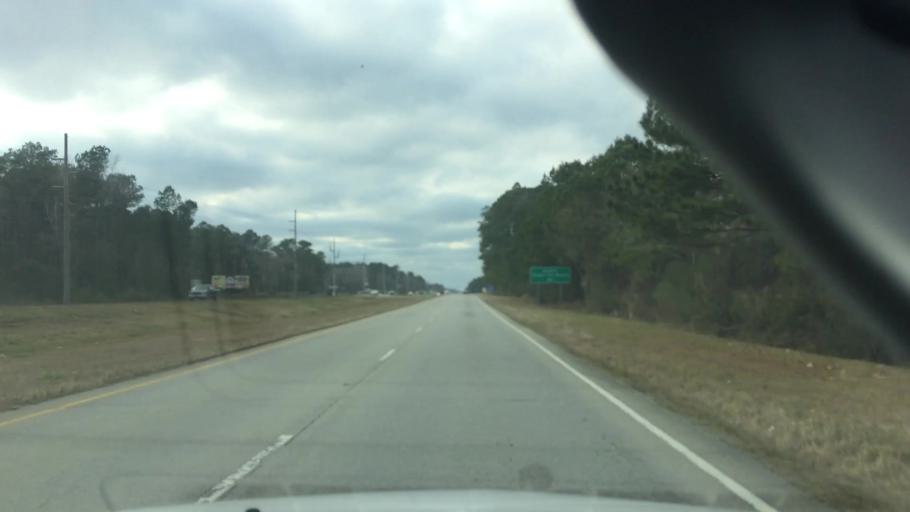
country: US
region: North Carolina
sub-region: Brunswick County
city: Shallotte
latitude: 33.9555
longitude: -78.4436
